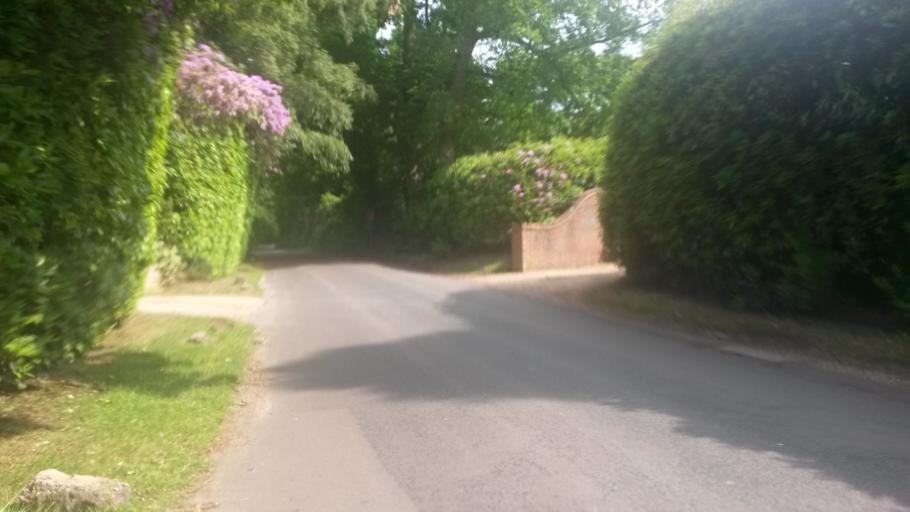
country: GB
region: England
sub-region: Surrey
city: Haslemere
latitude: 51.0796
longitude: -0.7023
